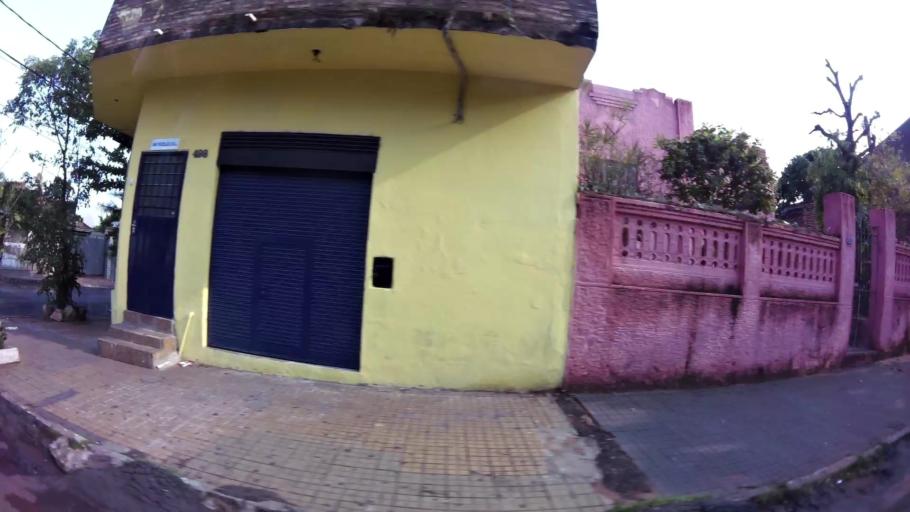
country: PY
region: Presidente Hayes
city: Nanawa
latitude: -25.2784
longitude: -57.6512
